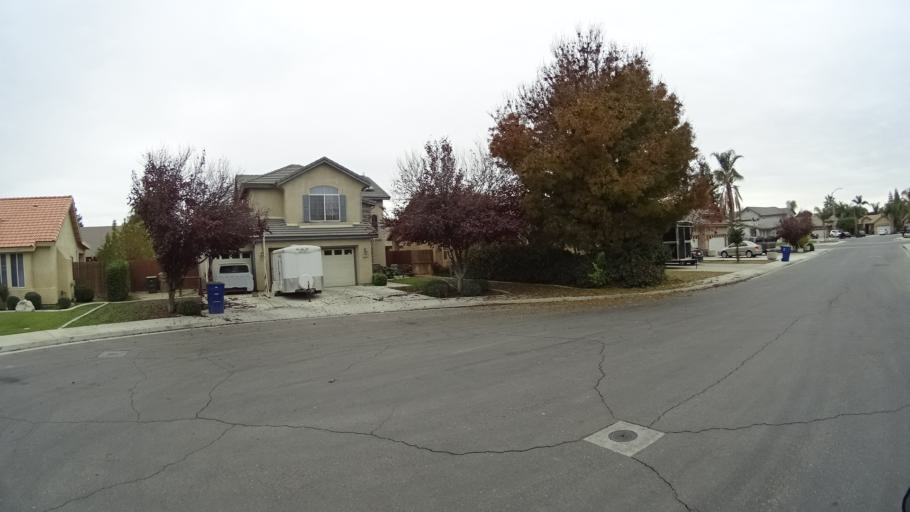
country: US
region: California
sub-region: Kern County
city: Greenfield
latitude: 35.2829
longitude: -119.0326
